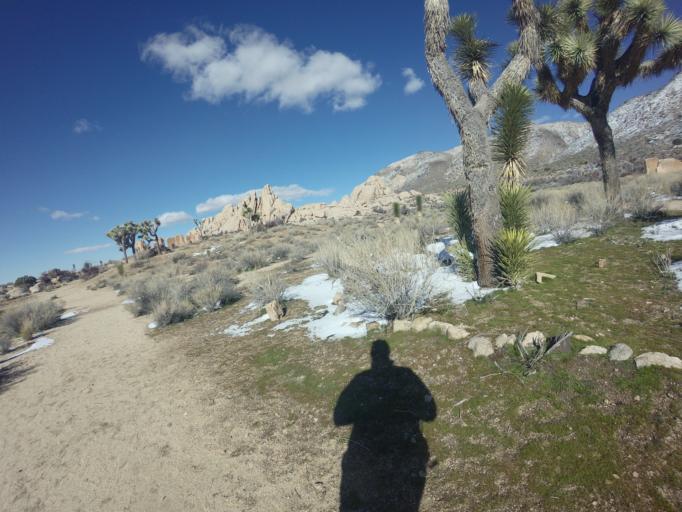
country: US
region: California
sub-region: San Bernardino County
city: Twentynine Palms
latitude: 33.9838
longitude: -116.1494
